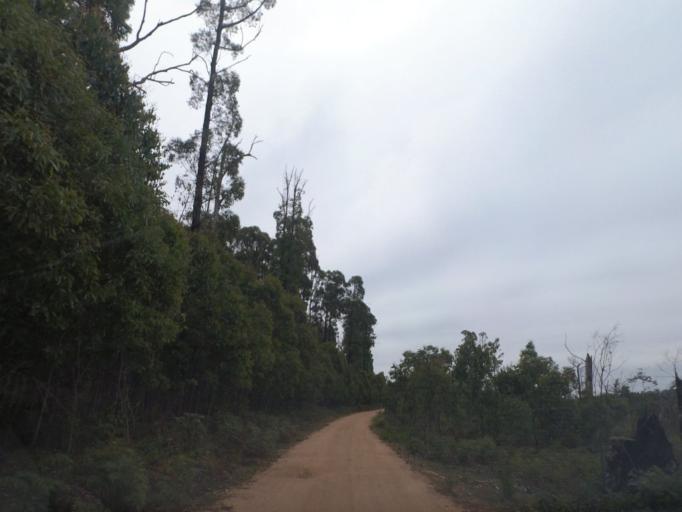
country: AU
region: Victoria
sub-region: Murrindindi
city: Alexandra
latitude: -37.4010
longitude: 145.5926
